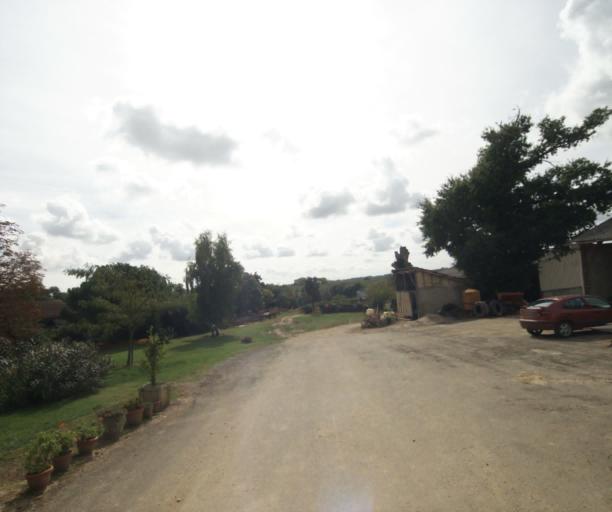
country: FR
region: Midi-Pyrenees
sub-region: Departement du Gers
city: Eauze
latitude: 43.8551
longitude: 0.0697
